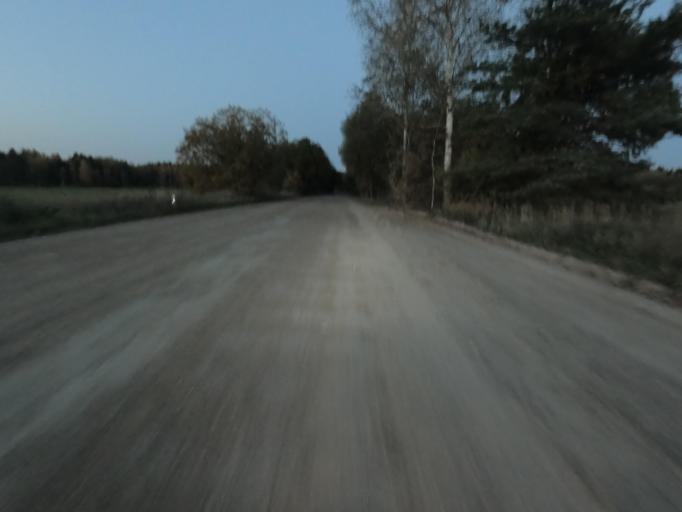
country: RU
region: Leningrad
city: Lyuban'
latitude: 59.1856
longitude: 31.2454
